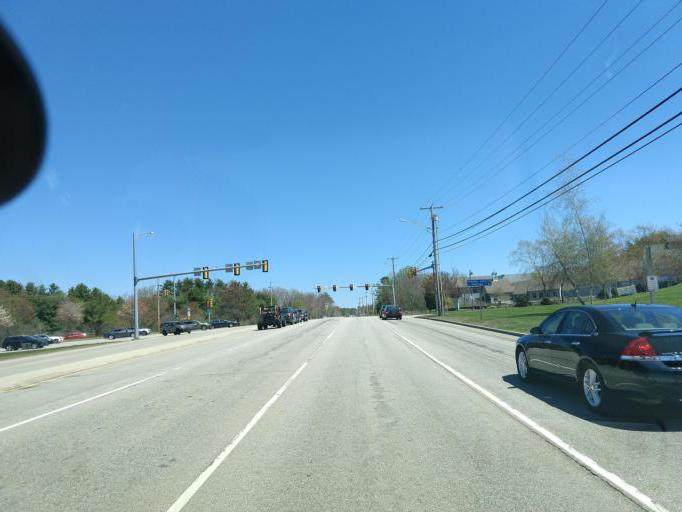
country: US
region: Maine
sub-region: York County
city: York Harbor
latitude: 43.1541
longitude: -70.6596
